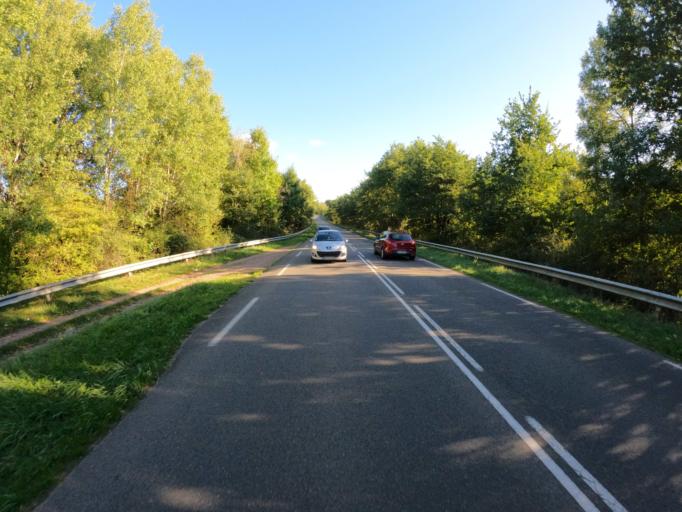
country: FR
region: Bourgogne
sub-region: Departement de Saone-et-Loire
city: Torcy
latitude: 46.7491
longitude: 4.4415
